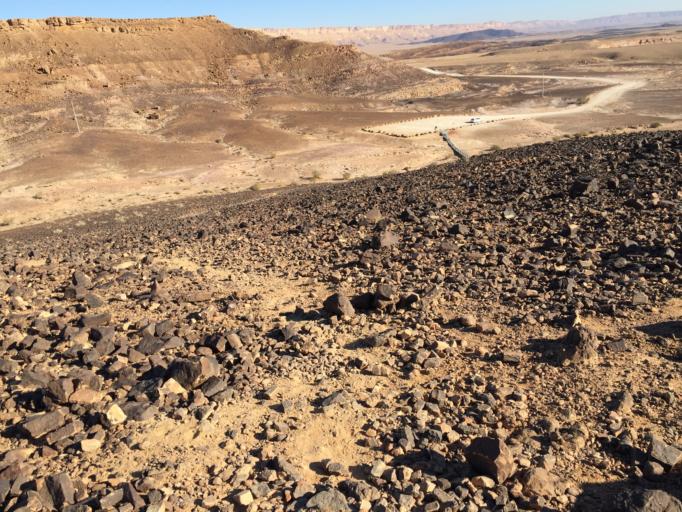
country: IL
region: Southern District
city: Mitzpe Ramon
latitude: 30.6175
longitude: 34.8401
